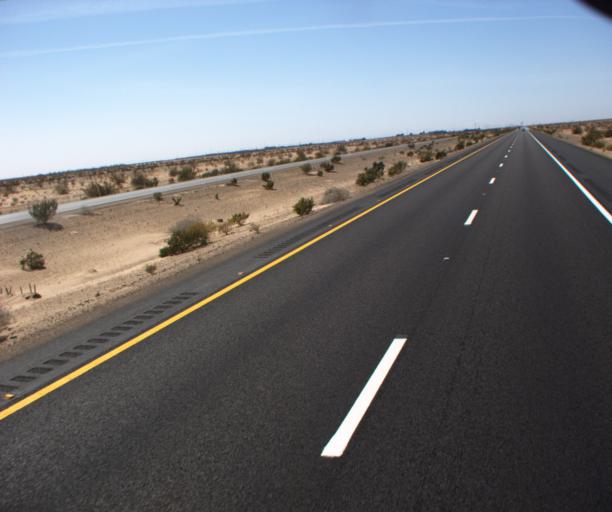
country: US
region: Arizona
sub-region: Yuma County
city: Somerton
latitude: 32.4954
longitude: -114.6217
